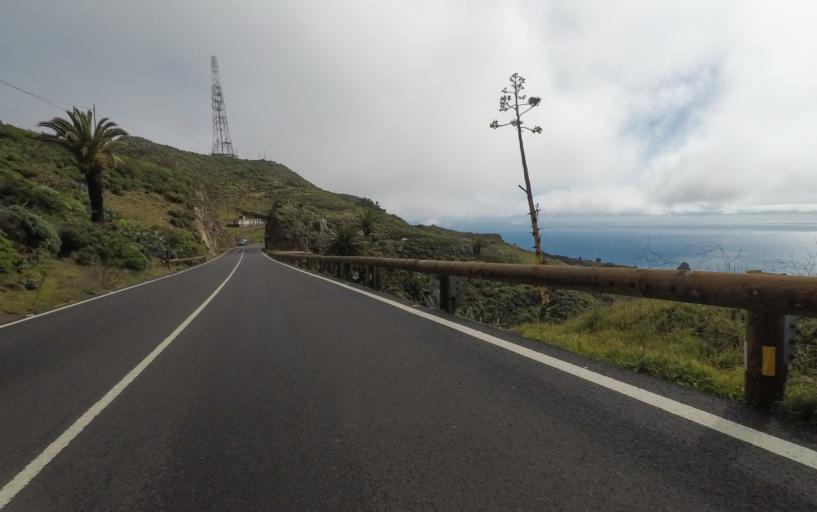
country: ES
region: Canary Islands
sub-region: Provincia de Santa Cruz de Tenerife
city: San Sebastian de la Gomera
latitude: 28.0982
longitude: -17.1818
